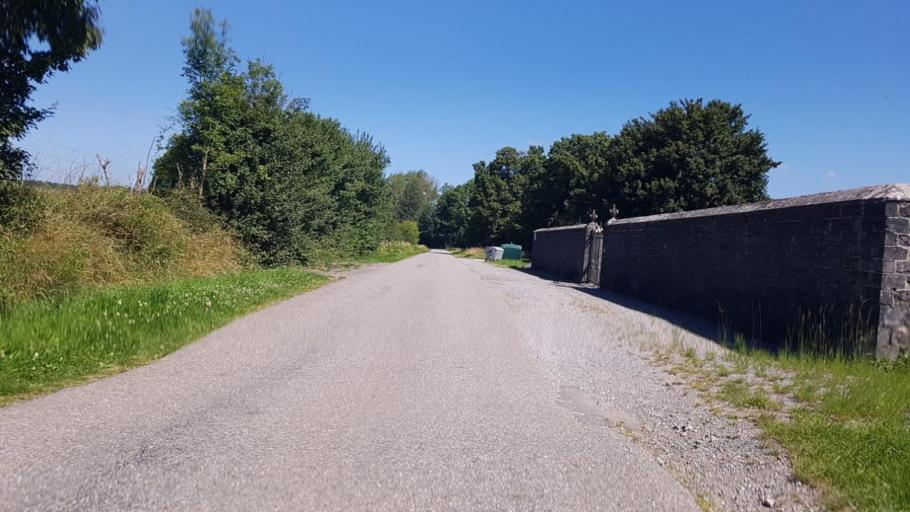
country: BE
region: Wallonia
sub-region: Province du Hainaut
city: Momignies
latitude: 50.0701
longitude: 4.2353
